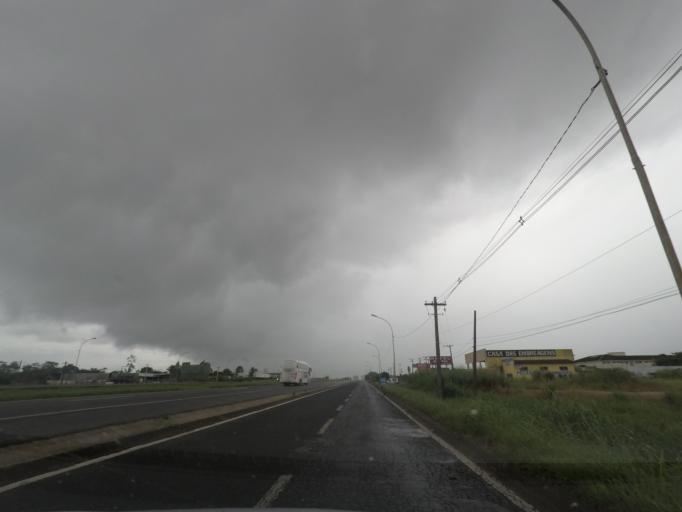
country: BR
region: Sao Paulo
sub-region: Registro
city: Registro
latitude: -24.5187
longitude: -47.8525
